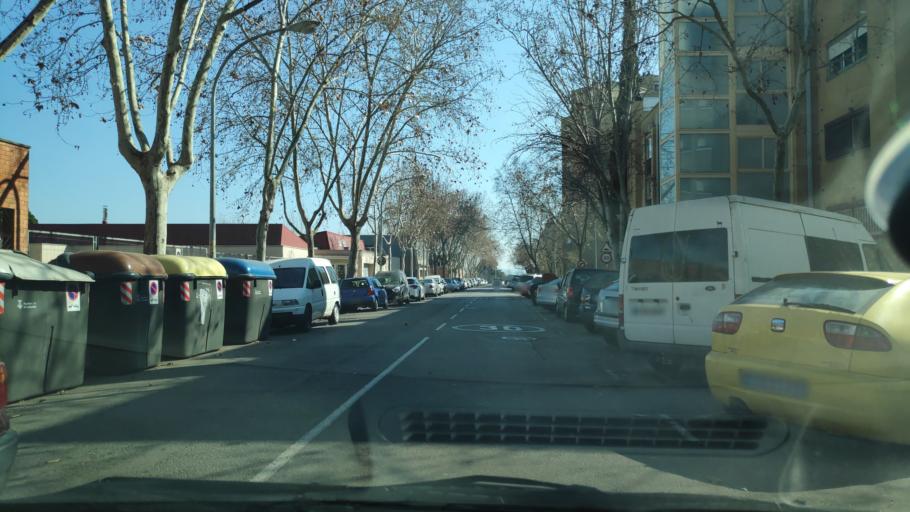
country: ES
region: Catalonia
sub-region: Provincia de Barcelona
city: Sant Quirze del Valles
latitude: 41.5433
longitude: 2.0890
